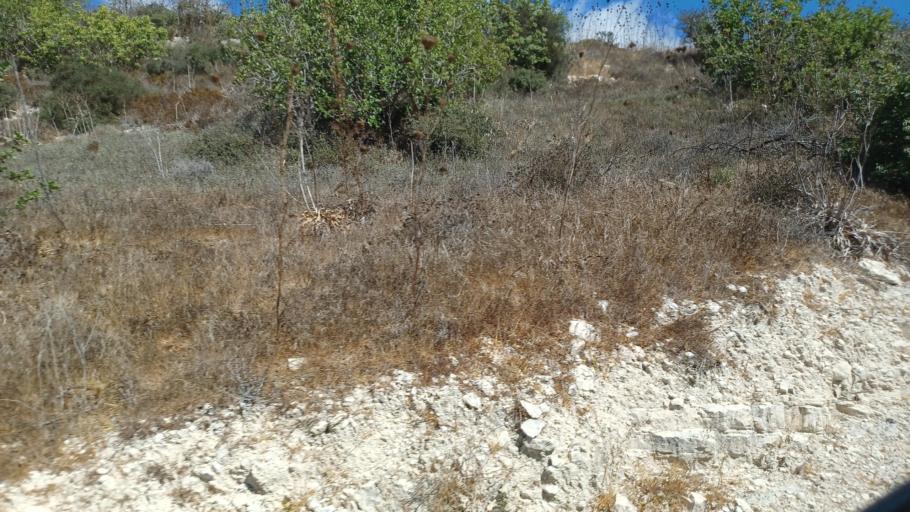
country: CY
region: Pafos
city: Tala
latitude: 34.8574
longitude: 32.4395
